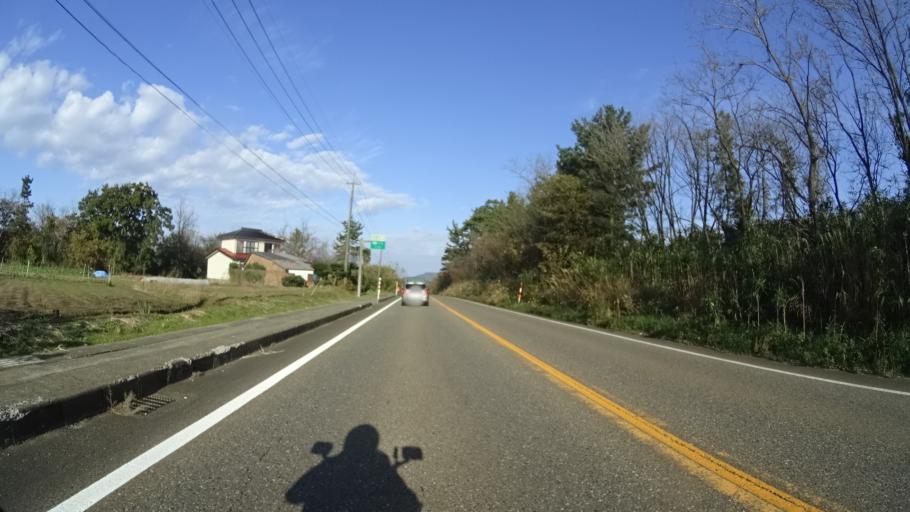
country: JP
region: Niigata
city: Joetsu
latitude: 37.2562
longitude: 138.3653
